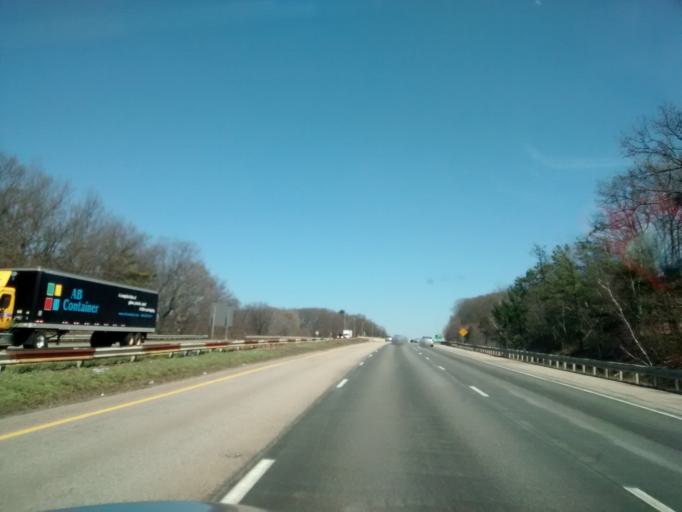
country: US
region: Massachusetts
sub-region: Worcester County
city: Millbury
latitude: 42.2219
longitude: -71.7505
